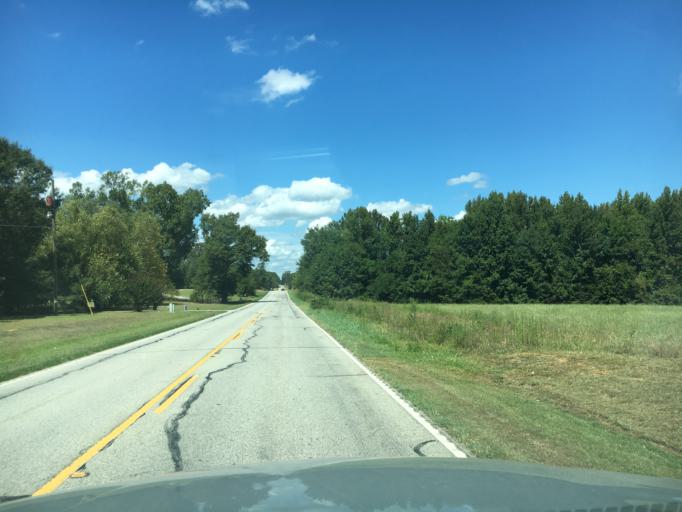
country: US
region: South Carolina
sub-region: Laurens County
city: Laurens
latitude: 34.5100
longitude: -82.0852
